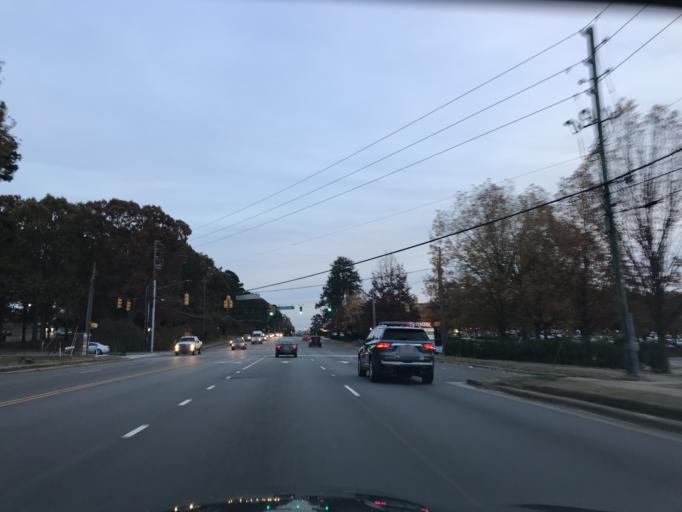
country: US
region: North Carolina
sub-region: Wake County
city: West Raleigh
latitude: 35.8759
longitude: -78.6236
